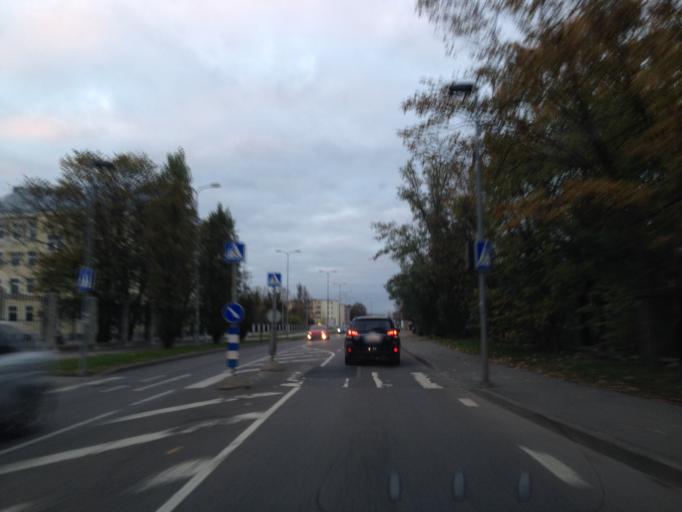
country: EE
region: Harju
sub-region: Tallinna linn
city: Tallinn
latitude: 59.4272
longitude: 24.8016
